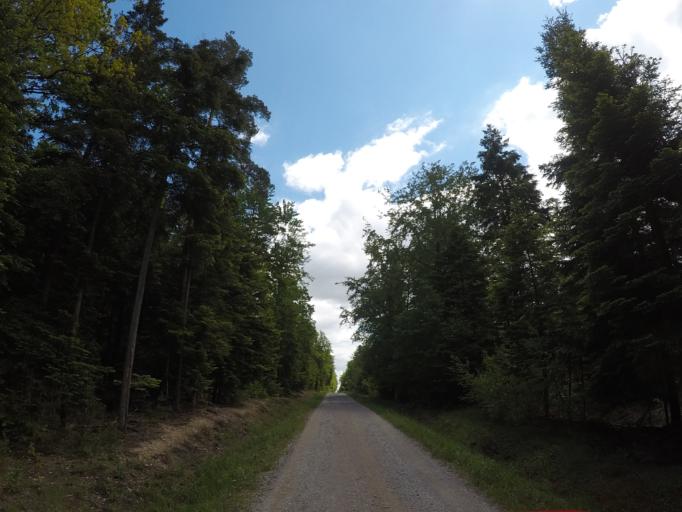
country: PL
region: Swietokrzyskie
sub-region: Powiat kielecki
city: Kielce
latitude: 50.9164
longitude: 20.6447
